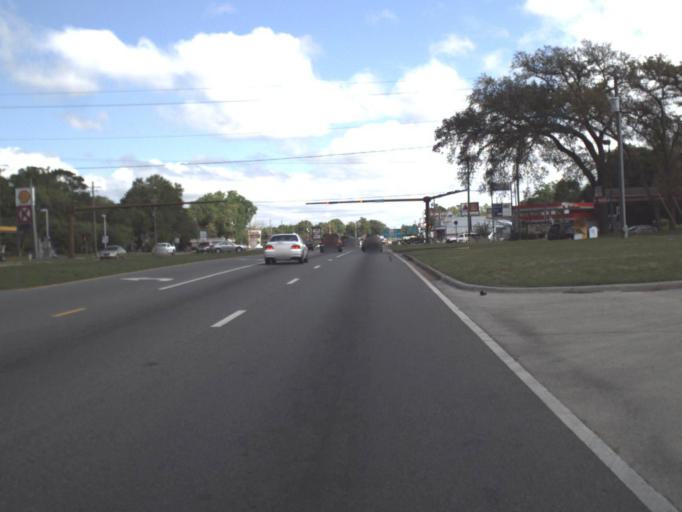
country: US
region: Florida
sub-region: Escambia County
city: West Pensacola
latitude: 30.4167
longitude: -87.2757
